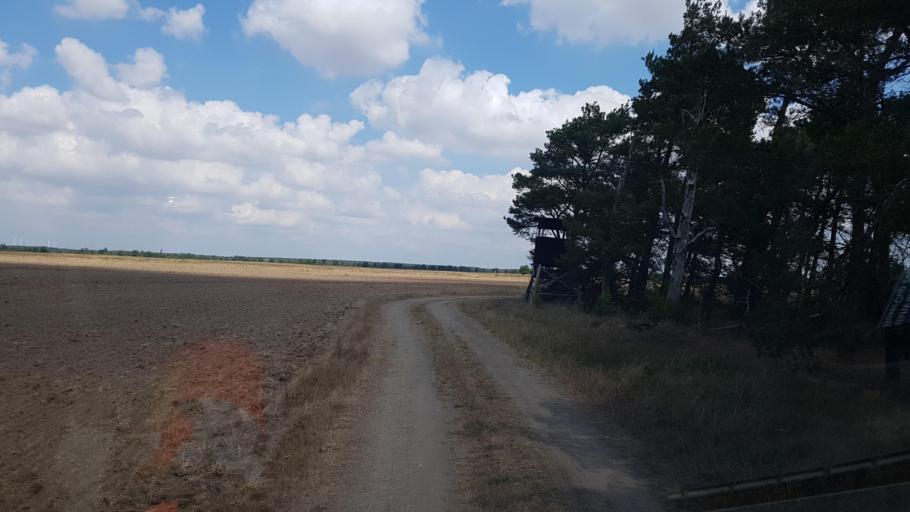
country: DE
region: Brandenburg
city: Muhlberg
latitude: 51.4162
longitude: 13.2992
